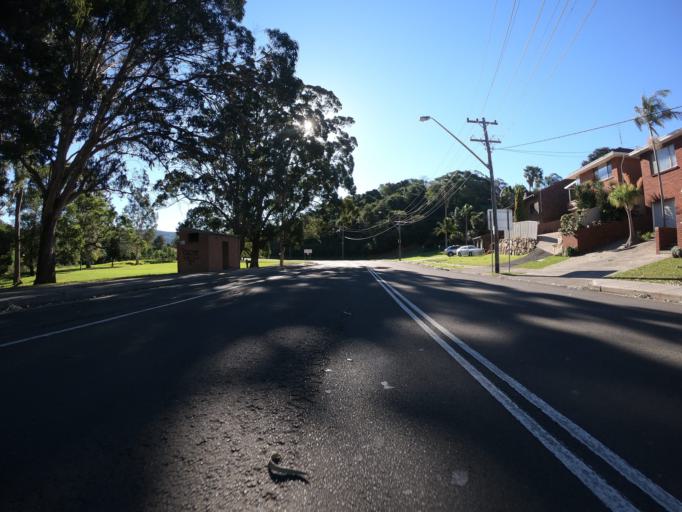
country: AU
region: New South Wales
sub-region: Wollongong
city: Mangerton
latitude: -34.4384
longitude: 150.8576
